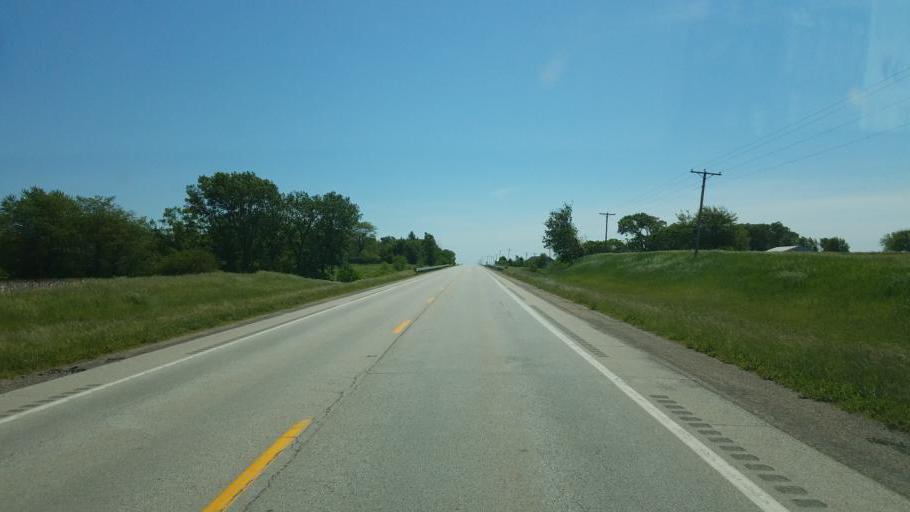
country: US
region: Illinois
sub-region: McLean County
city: Heyworth
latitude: 40.3122
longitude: -88.9536
